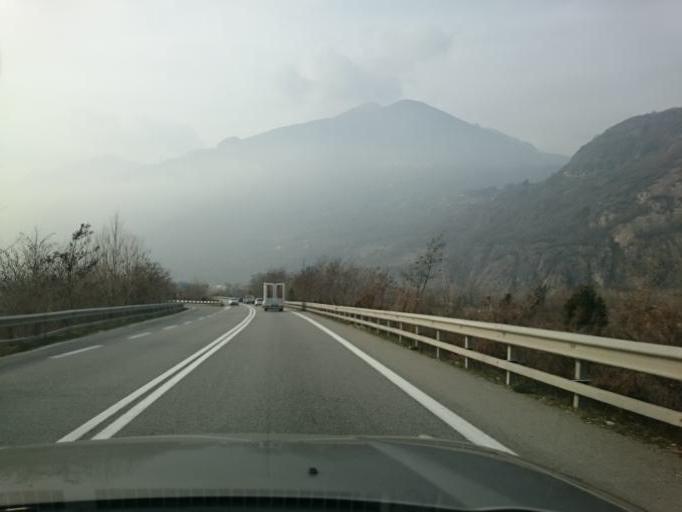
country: IT
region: Lombardy
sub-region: Provincia di Brescia
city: Gianico
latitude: 45.8722
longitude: 10.1672
